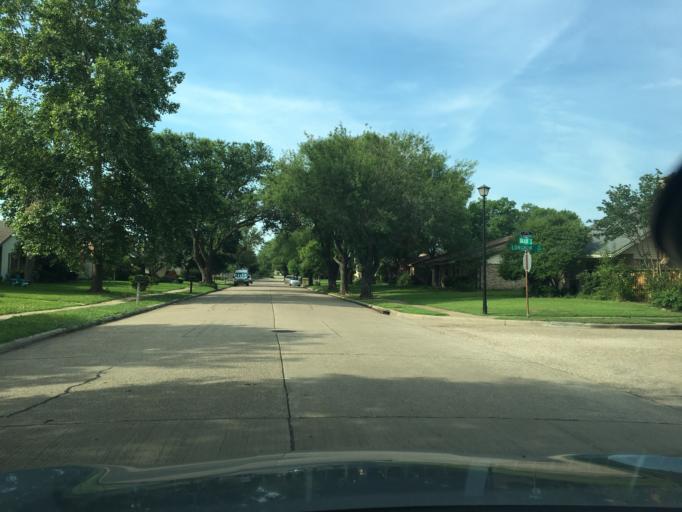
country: US
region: Texas
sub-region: Dallas County
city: Richardson
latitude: 32.9640
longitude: -96.6733
